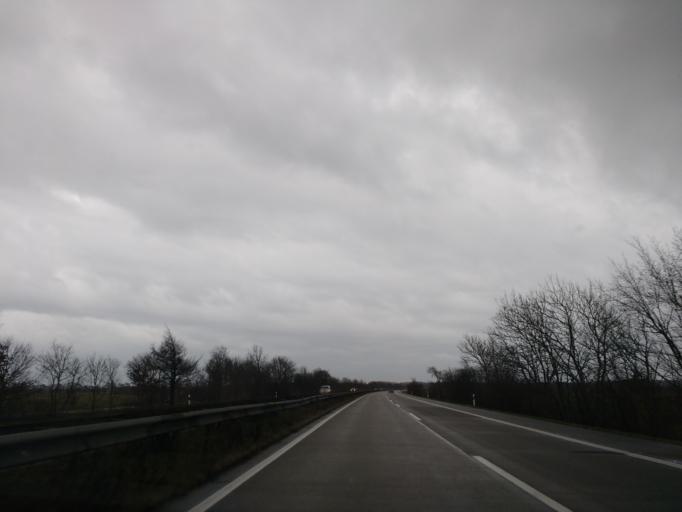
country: DE
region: Lower Saxony
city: Midlum
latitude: 53.7740
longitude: 8.7032
